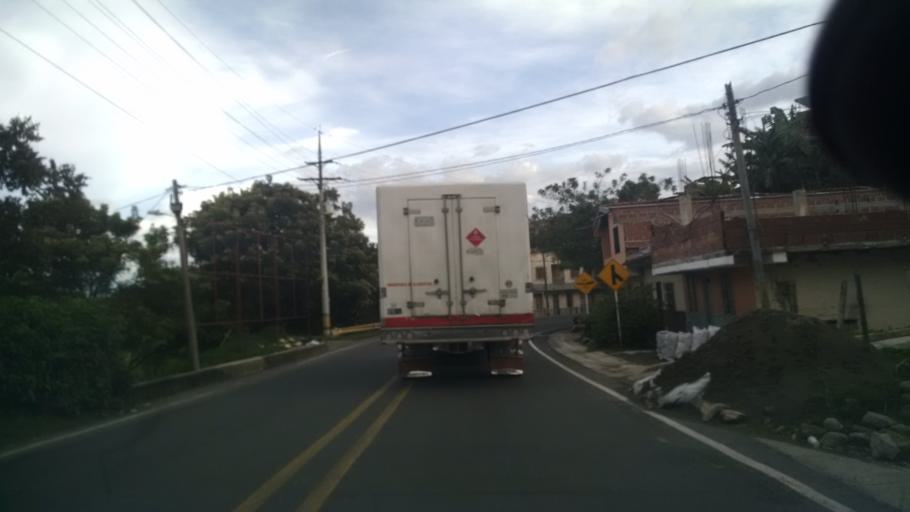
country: CO
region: Antioquia
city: Santa Barbara
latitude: 5.8764
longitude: -75.5659
